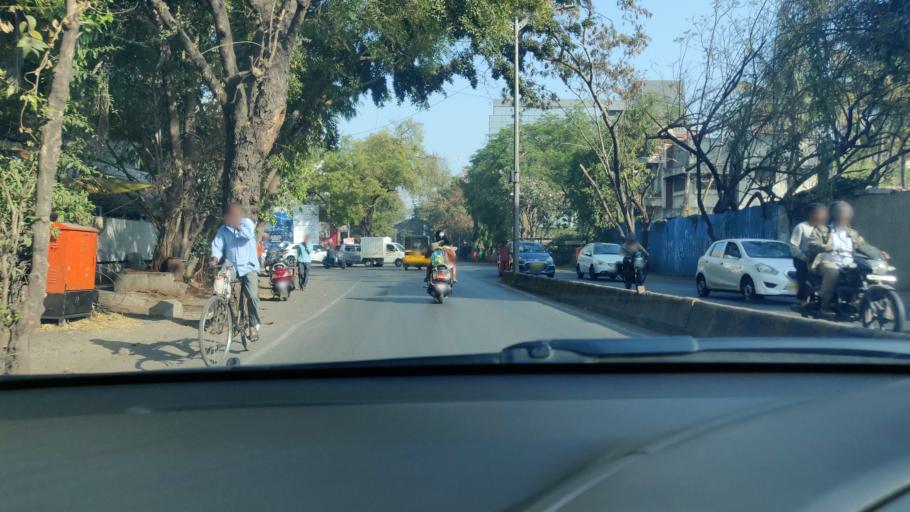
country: IN
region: Maharashtra
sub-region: Pune Division
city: Khadki
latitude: 18.5529
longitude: 73.8095
